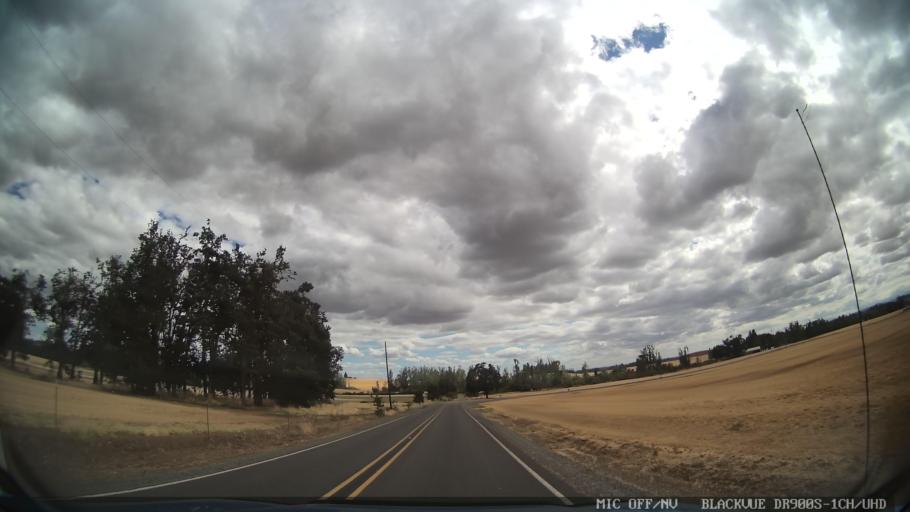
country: US
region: Oregon
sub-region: Marion County
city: Sublimity
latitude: 44.8459
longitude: -122.7537
